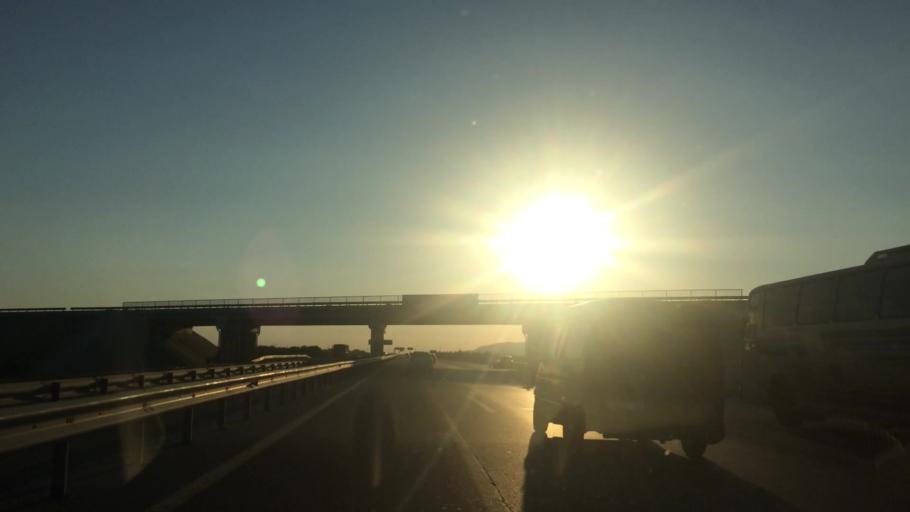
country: AZ
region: Baki
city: Qobustan
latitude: 39.9542
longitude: 49.3786
